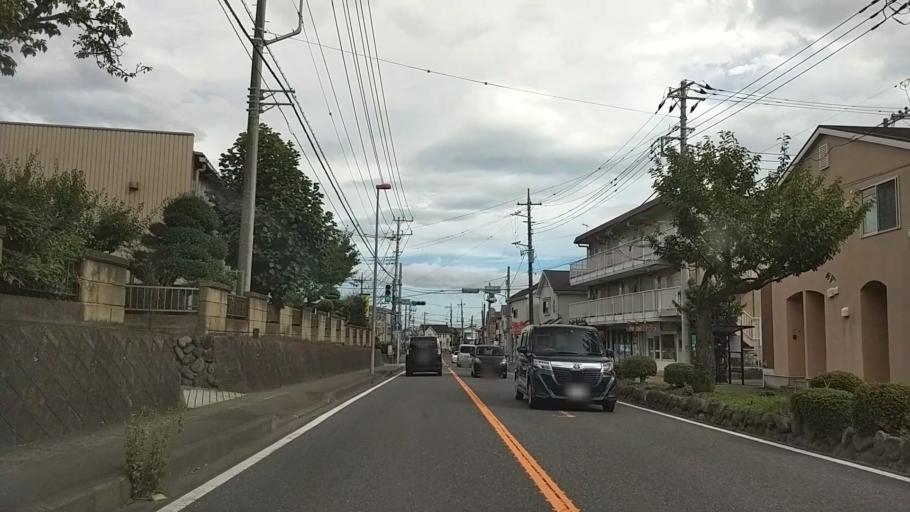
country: JP
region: Tokyo
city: Hachioji
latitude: 35.5869
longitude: 139.3172
